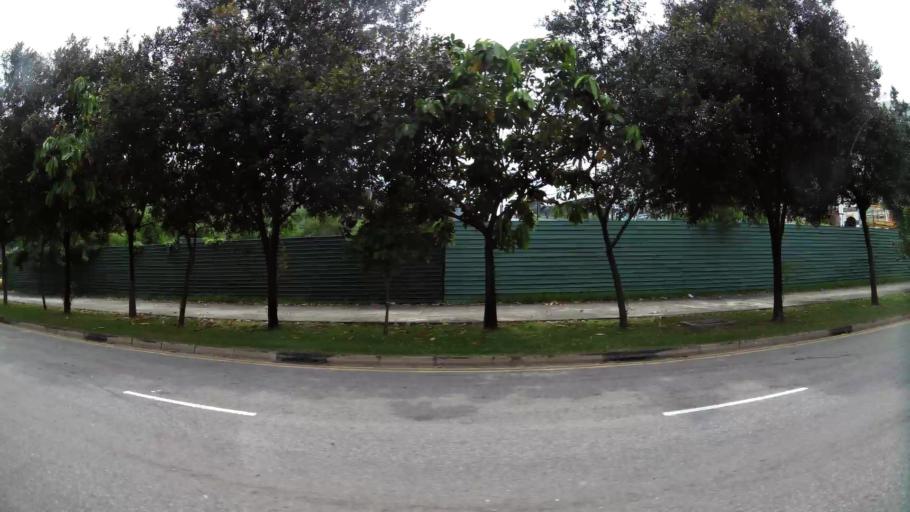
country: SG
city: Singapore
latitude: 1.3140
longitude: 103.7000
